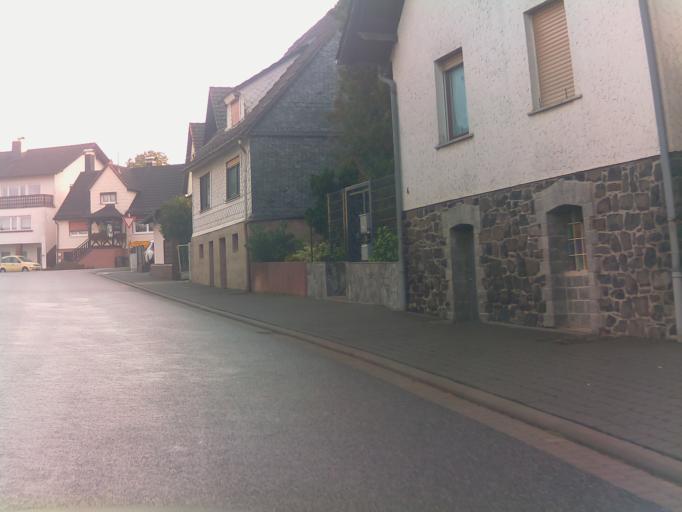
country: DE
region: Hesse
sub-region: Regierungsbezirk Darmstadt
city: Hirzenhain
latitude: 50.4166
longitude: 9.1339
